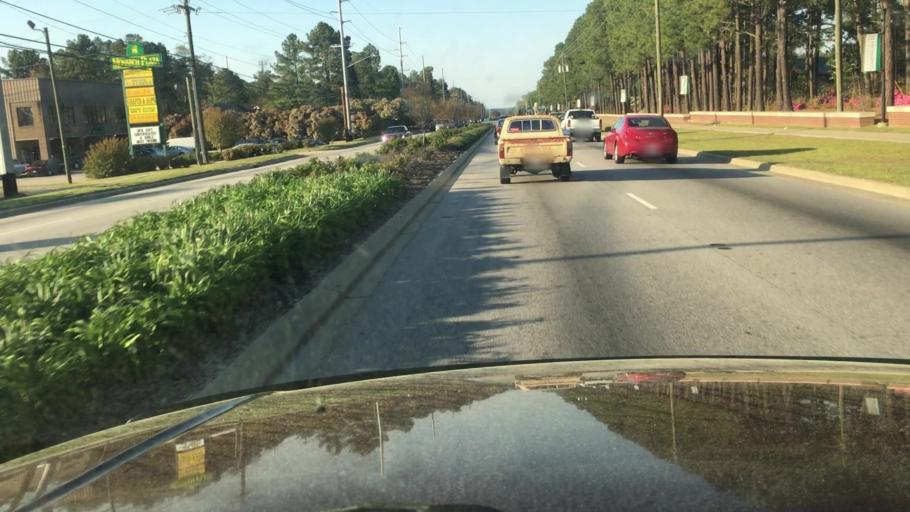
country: US
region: North Carolina
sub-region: Cumberland County
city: Fayetteville
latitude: 35.1332
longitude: -78.8771
